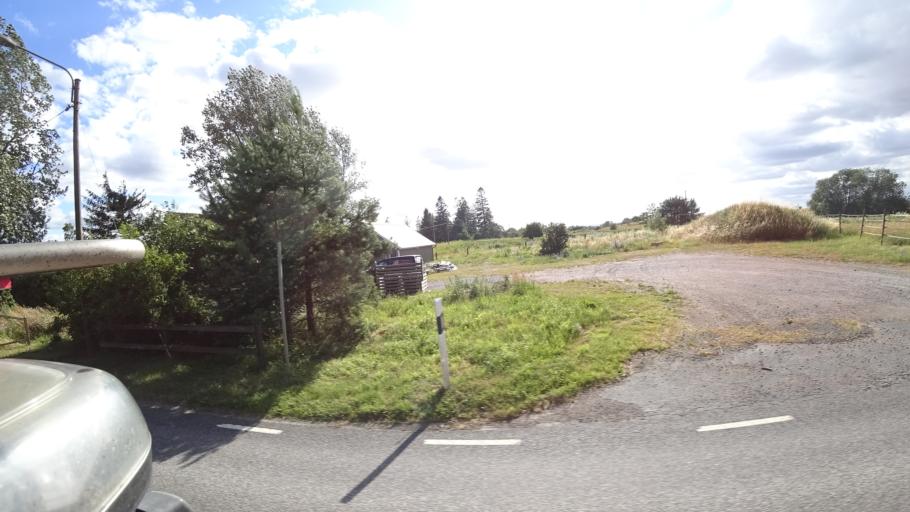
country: SE
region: Skane
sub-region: Kristianstads Kommun
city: Onnestad
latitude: 56.0816
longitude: 14.0814
